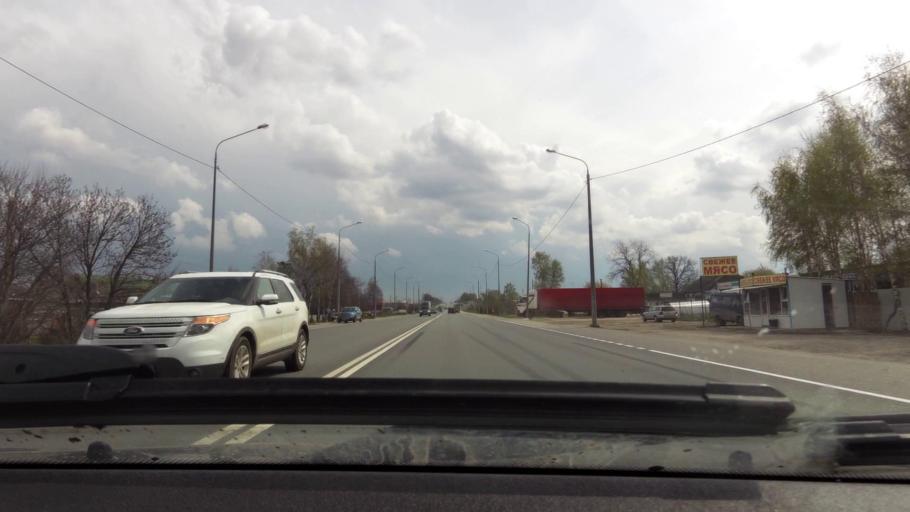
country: RU
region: Rjazan
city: Bagramovo
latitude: 54.7321
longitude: 39.4603
